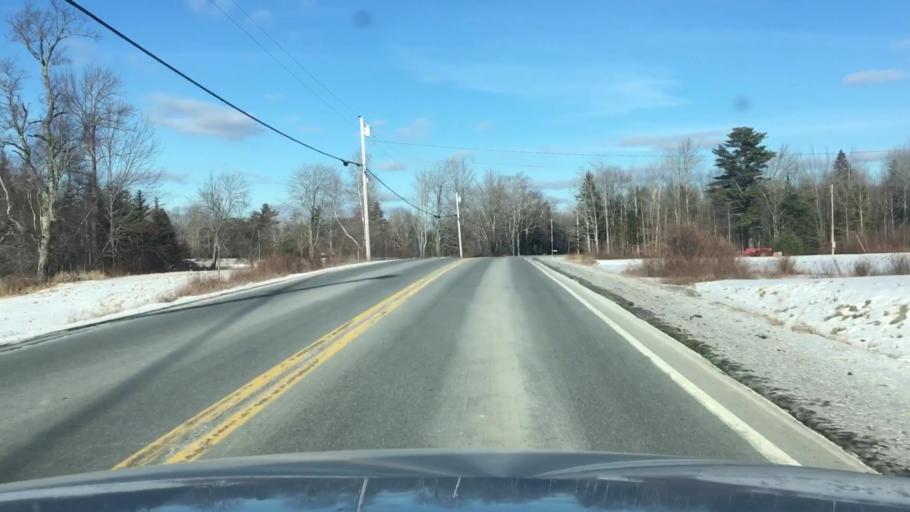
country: US
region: Maine
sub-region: Penobscot County
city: Holden
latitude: 44.7650
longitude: -68.5942
